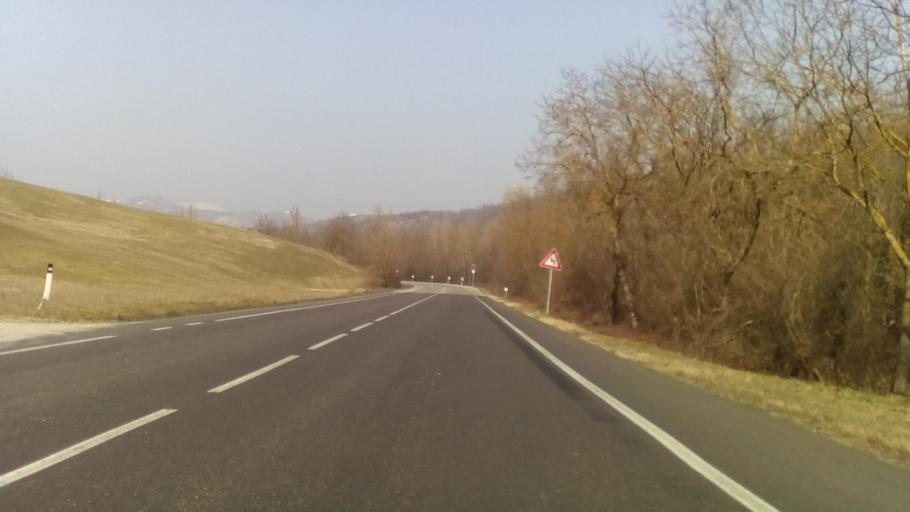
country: IT
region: Emilia-Romagna
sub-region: Provincia di Modena
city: Serramazzoni
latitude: 44.4420
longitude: 10.8347
